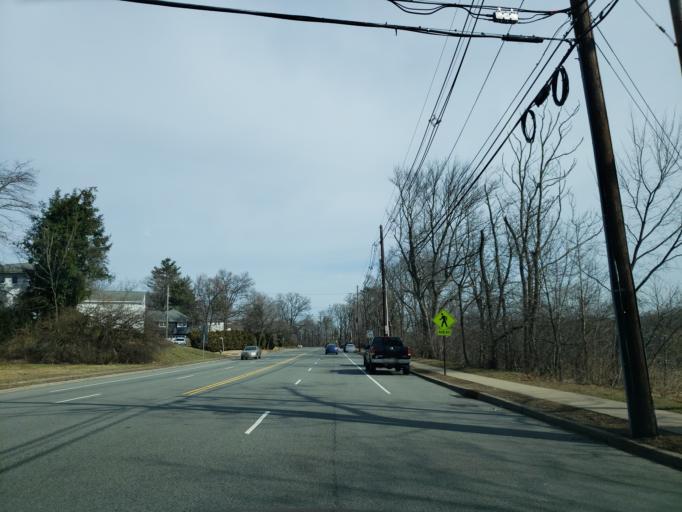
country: US
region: New Jersey
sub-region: Essex County
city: Verona
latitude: 40.8254
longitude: -74.2499
